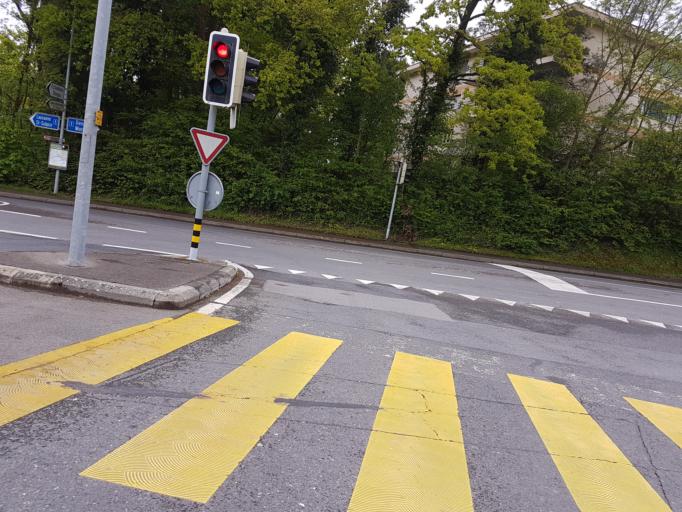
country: CH
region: Vaud
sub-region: Morges District
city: Preverenges
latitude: 46.5141
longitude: 6.5412
